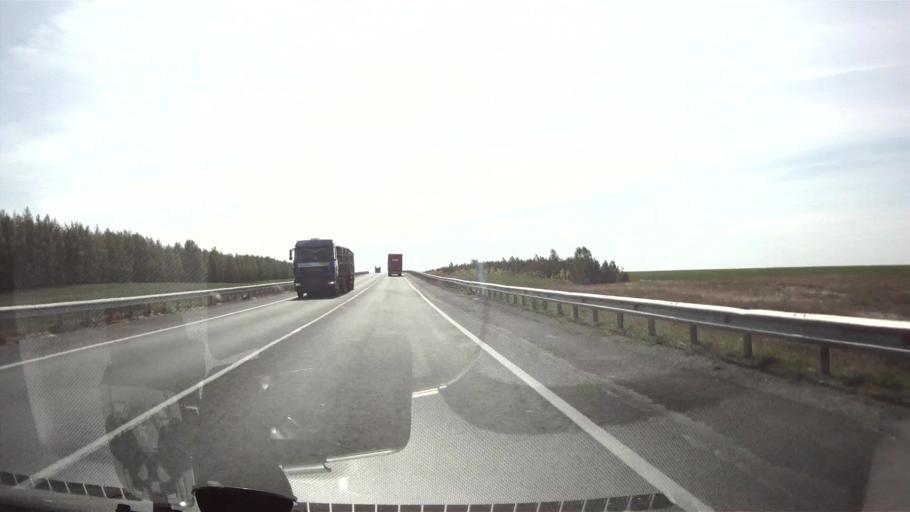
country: RU
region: Samara
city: Syzran'
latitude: 52.8995
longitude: 48.2960
